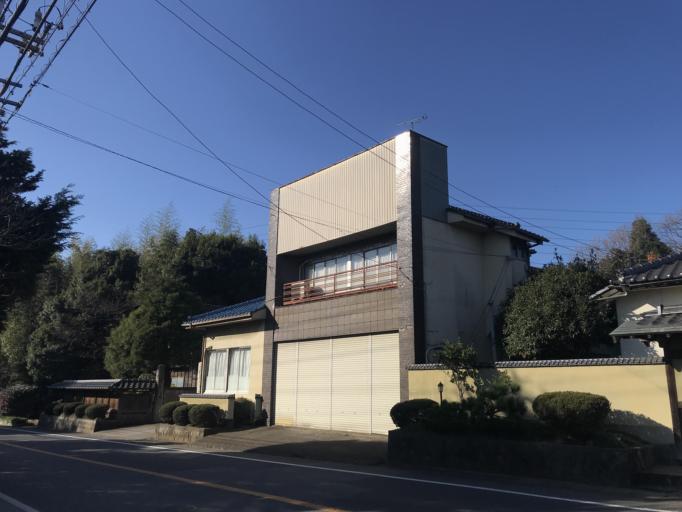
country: JP
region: Tochigi
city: Oyama
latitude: 36.2101
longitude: 139.8228
